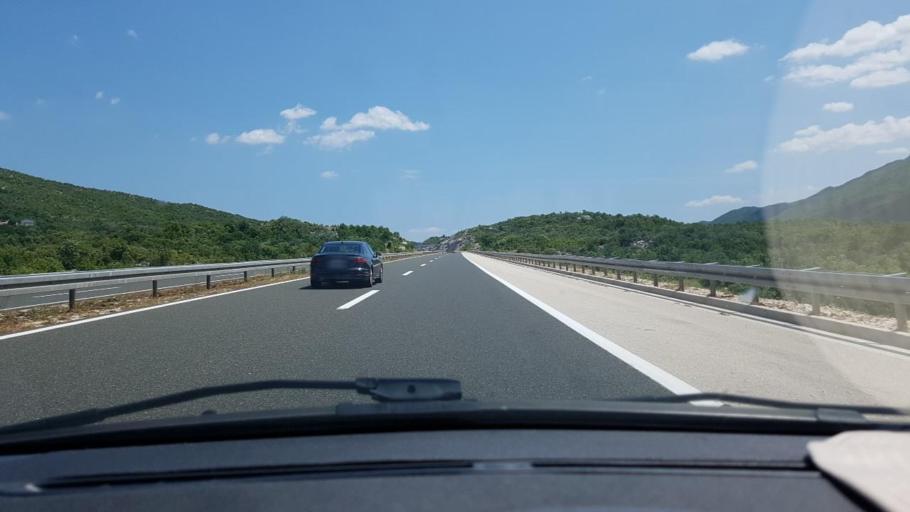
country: HR
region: Splitsko-Dalmatinska
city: Grubine
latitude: 43.3842
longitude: 17.0692
